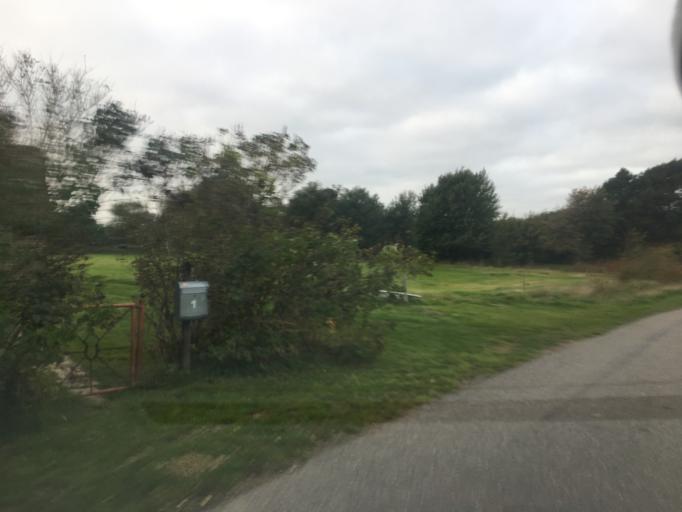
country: DE
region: Schleswig-Holstein
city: Rodenas
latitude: 54.9707
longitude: 8.7435
